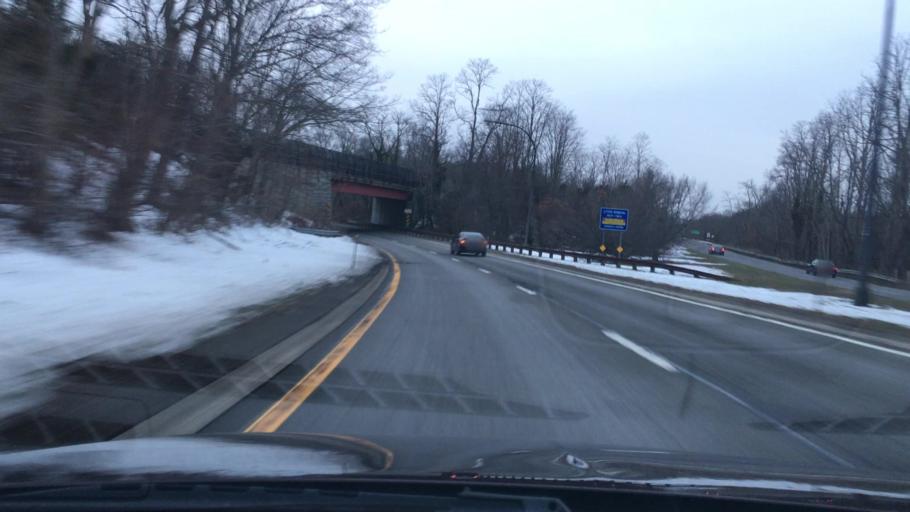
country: US
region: New York
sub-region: Suffolk County
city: Commack
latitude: 40.8301
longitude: -73.2530
